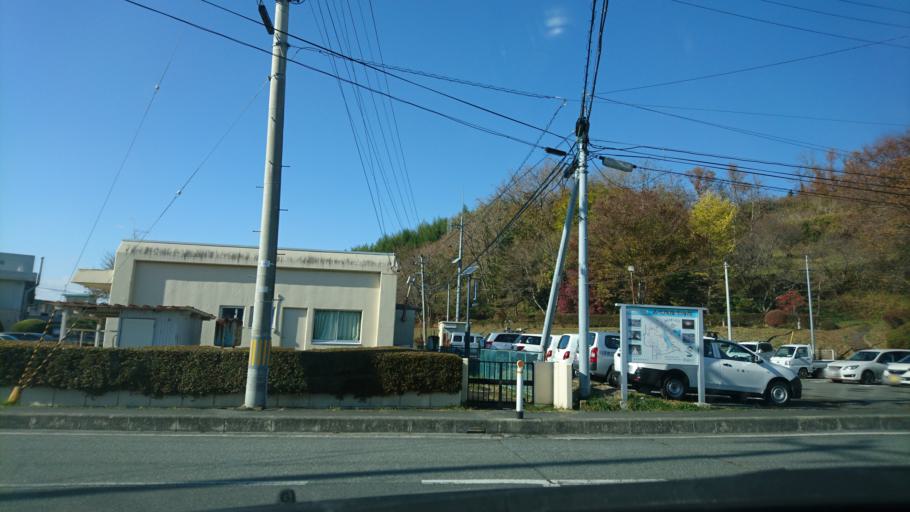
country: JP
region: Iwate
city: Ichinoseki
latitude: 39.0171
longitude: 141.3962
